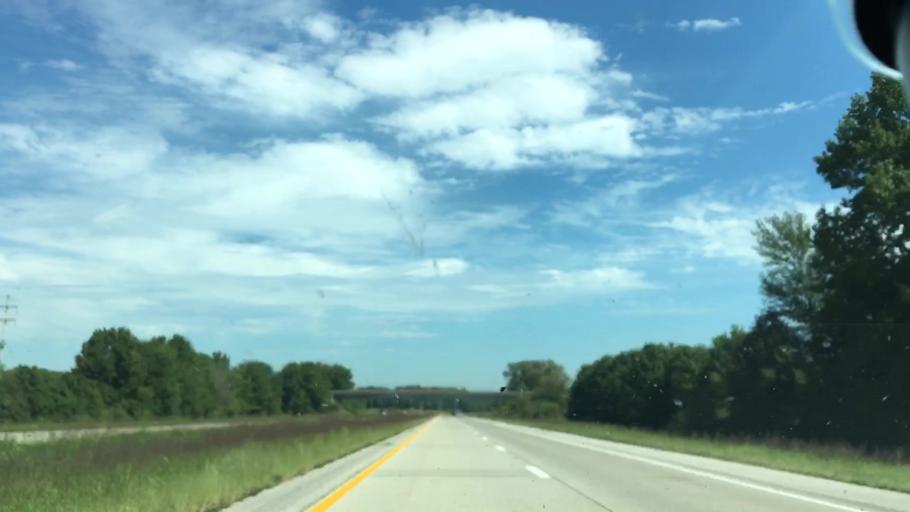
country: US
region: Kentucky
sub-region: Daviess County
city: Owensboro
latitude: 37.7664
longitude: -87.2145
